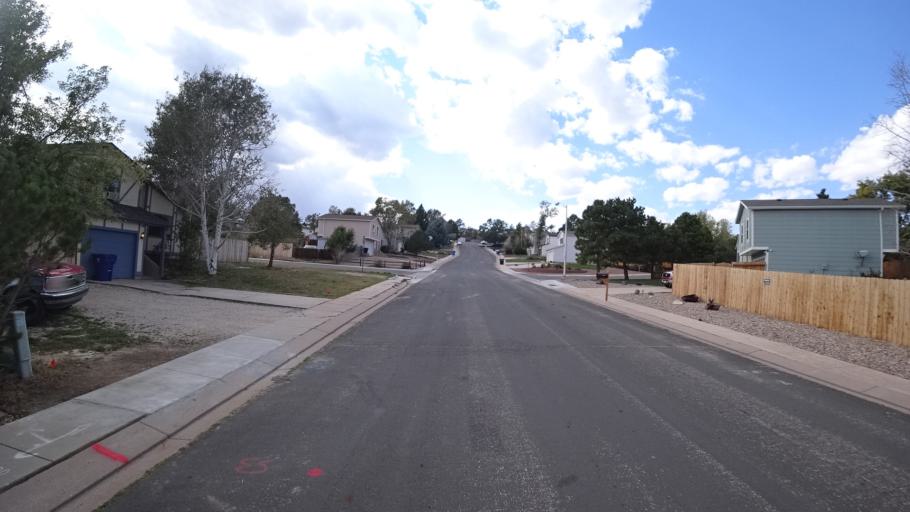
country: US
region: Colorado
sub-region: El Paso County
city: Cimarron Hills
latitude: 38.8755
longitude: -104.7248
